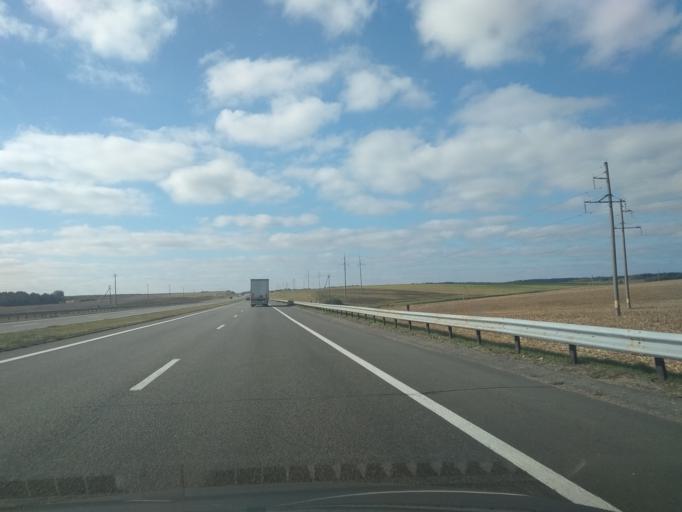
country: BY
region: Minsk
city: Stowbtsy
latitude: 53.5228
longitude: 26.7114
